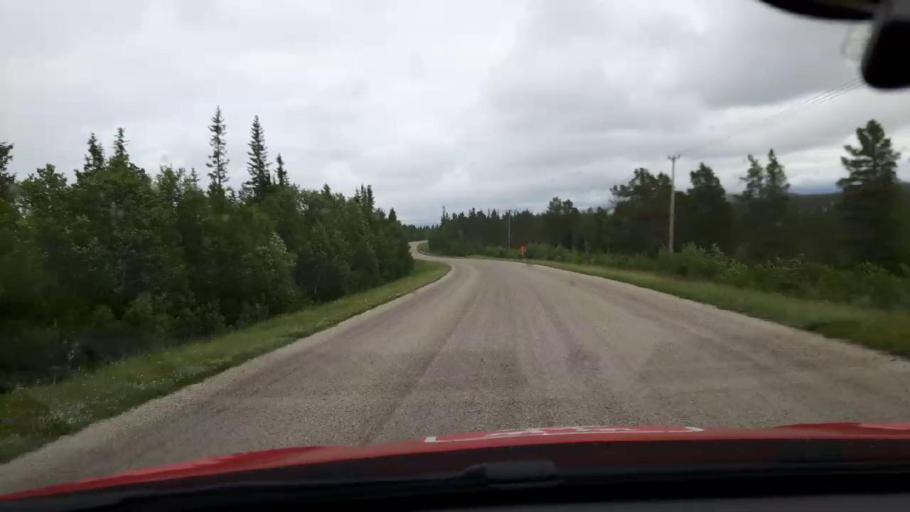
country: NO
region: Nord-Trondelag
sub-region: Meraker
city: Meraker
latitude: 63.2697
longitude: 12.3731
